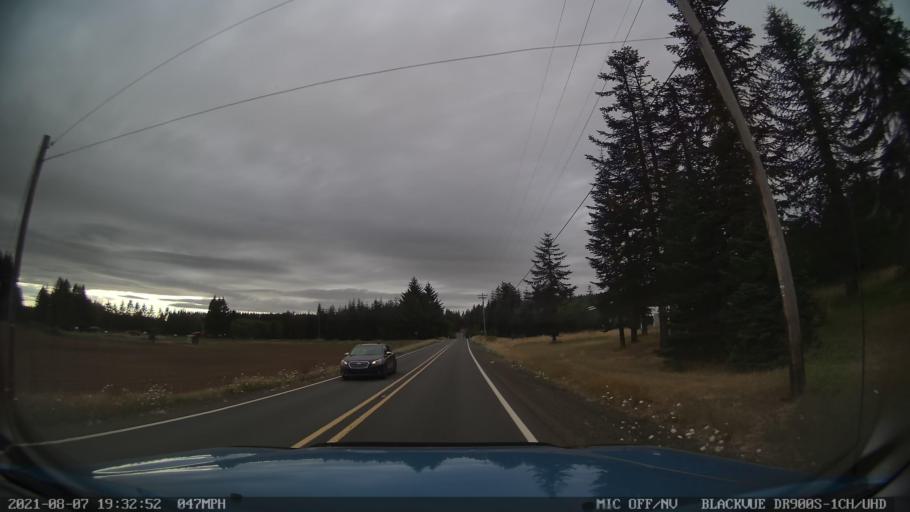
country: US
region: Oregon
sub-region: Linn County
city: Lyons
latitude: 44.9033
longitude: -122.6487
